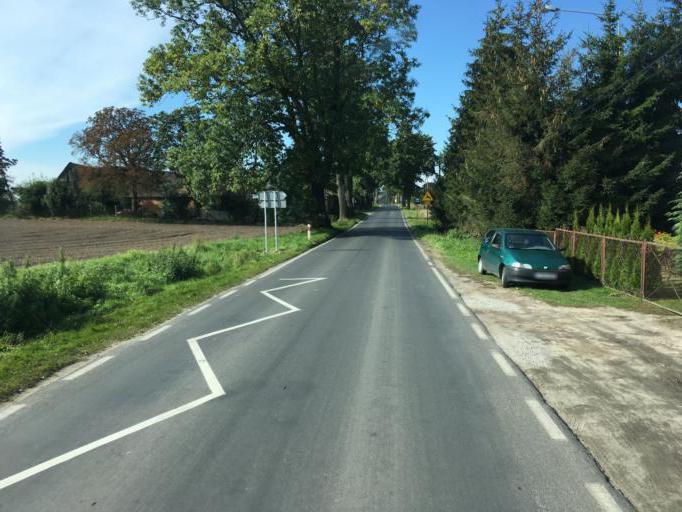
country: PL
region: Kujawsko-Pomorskie
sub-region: Powiat swiecki
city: Lniano
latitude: 53.5205
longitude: 18.1964
